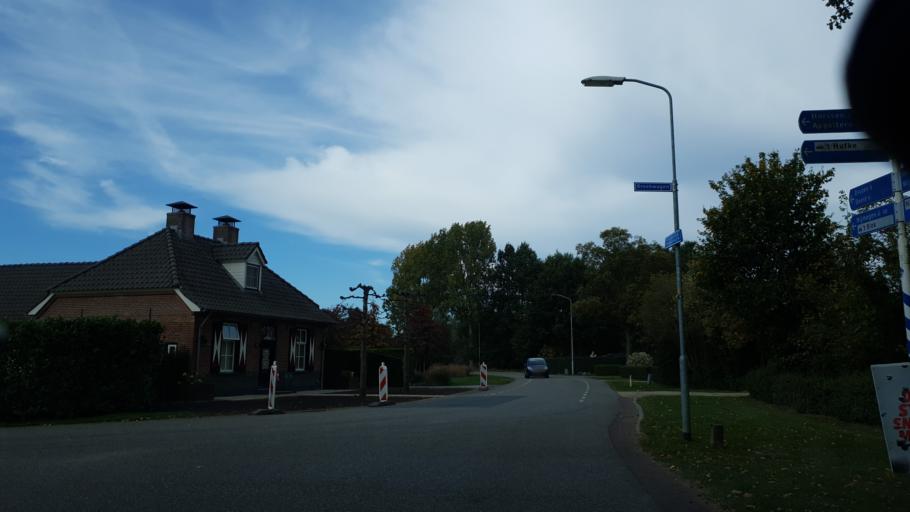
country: NL
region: Gelderland
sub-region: Gemeente Wijchen
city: Bergharen
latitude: 51.8514
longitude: 5.6596
